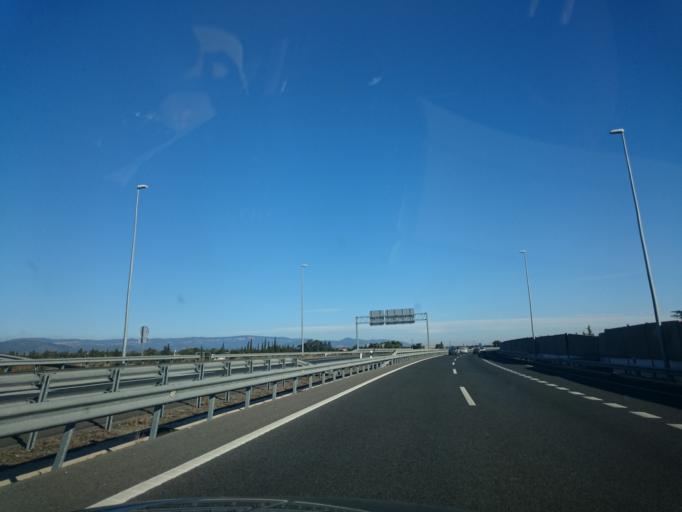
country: ES
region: Catalonia
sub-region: Provincia de Tarragona
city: Cambrils
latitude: 41.0601
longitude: 0.9921
